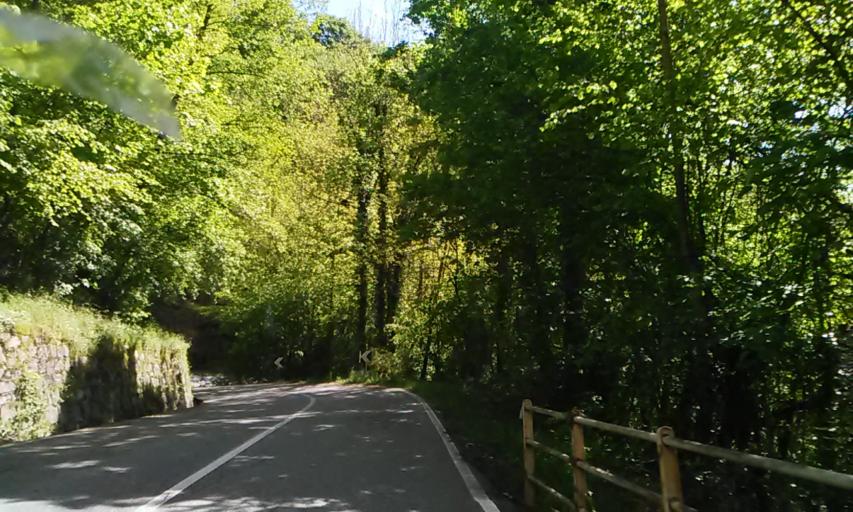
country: IT
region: Piedmont
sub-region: Provincia di Vercelli
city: Cellio
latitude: 45.7370
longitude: 8.3035
